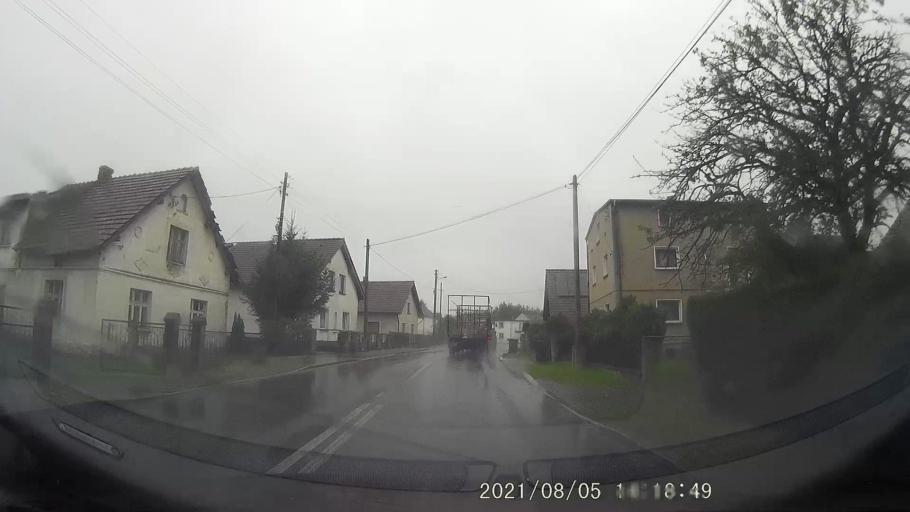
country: PL
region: Opole Voivodeship
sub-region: Powiat prudnicki
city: Biala
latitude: 50.4648
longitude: 17.6916
